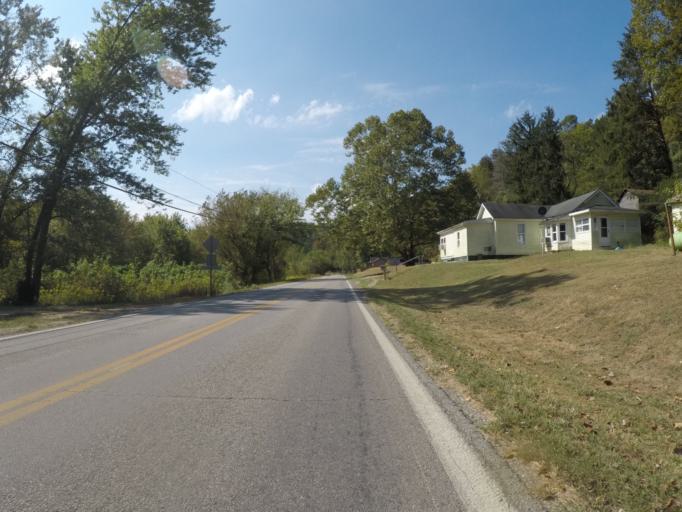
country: US
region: West Virginia
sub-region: Cabell County
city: Lesage
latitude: 38.5499
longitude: -82.3912
